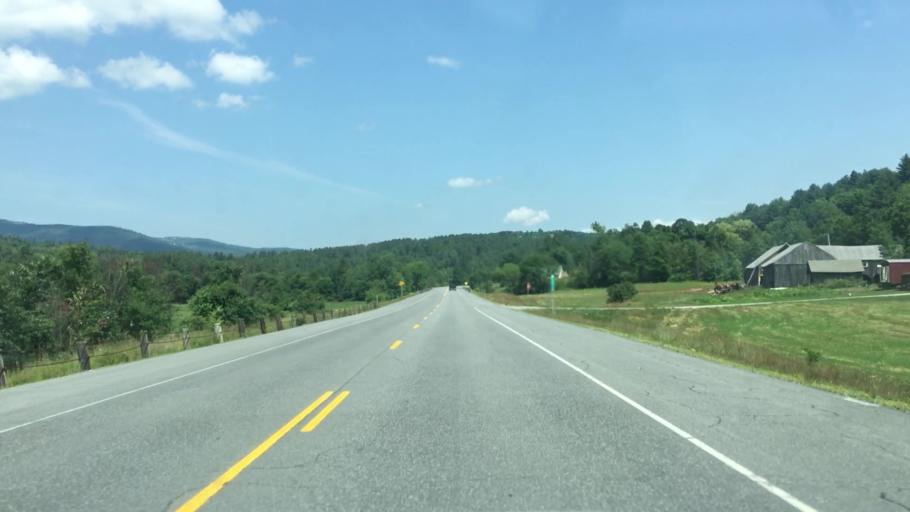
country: US
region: New Hampshire
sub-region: Sullivan County
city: Grantham
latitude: 43.4699
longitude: -72.1483
